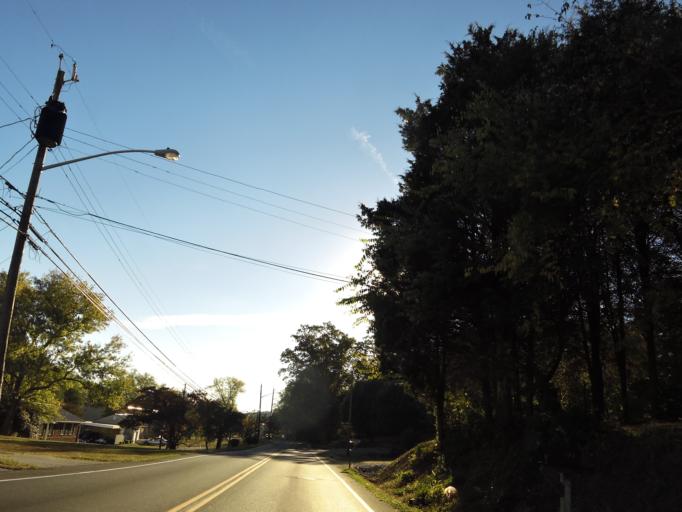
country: US
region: Tennessee
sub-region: Knox County
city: Knoxville
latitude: 36.0073
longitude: -83.9502
